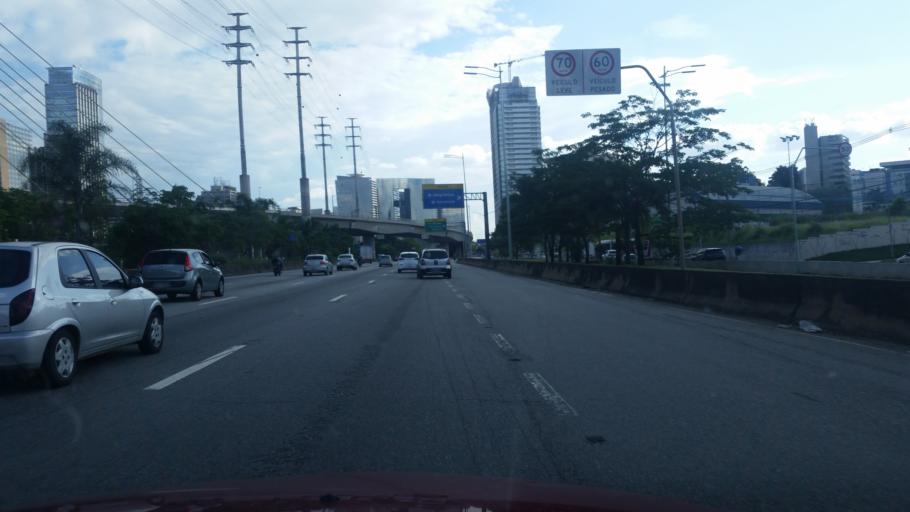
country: BR
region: Sao Paulo
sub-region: Sao Paulo
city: Sao Paulo
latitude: -23.6117
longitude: -46.7004
